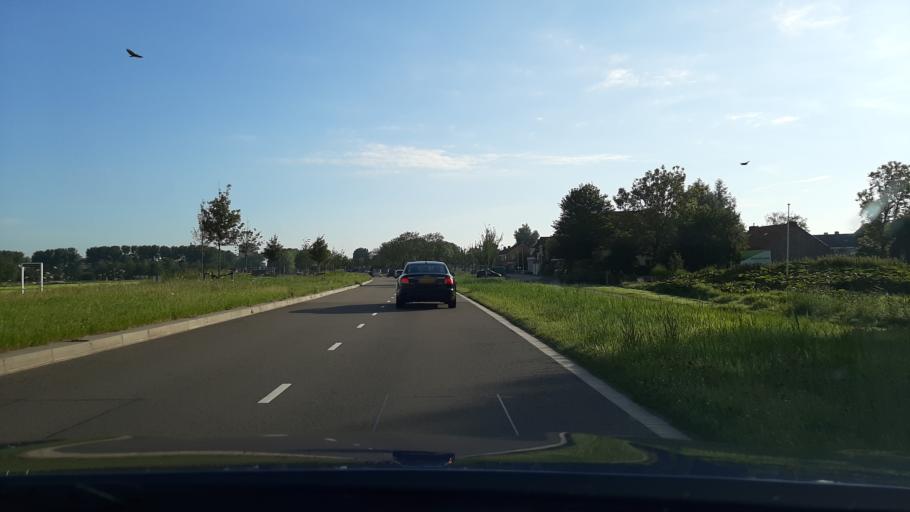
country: NL
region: Friesland
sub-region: Gemeente Leeuwarden
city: Goutum
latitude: 53.1739
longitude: 5.7932
